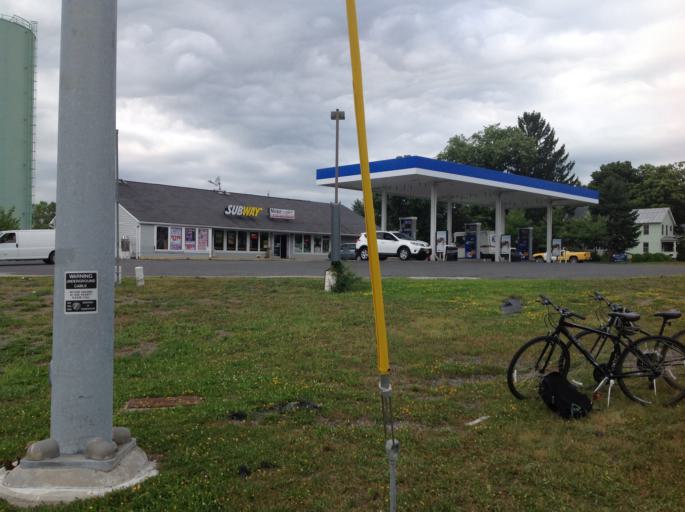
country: US
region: New York
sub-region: Columbia County
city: Stottville
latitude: 42.2830
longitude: -73.7559
